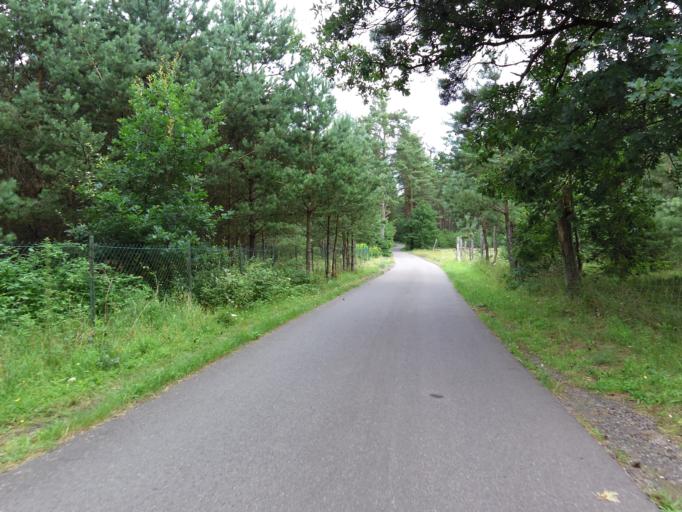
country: DE
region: Brandenburg
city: Lychen
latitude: 53.2268
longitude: 13.2745
